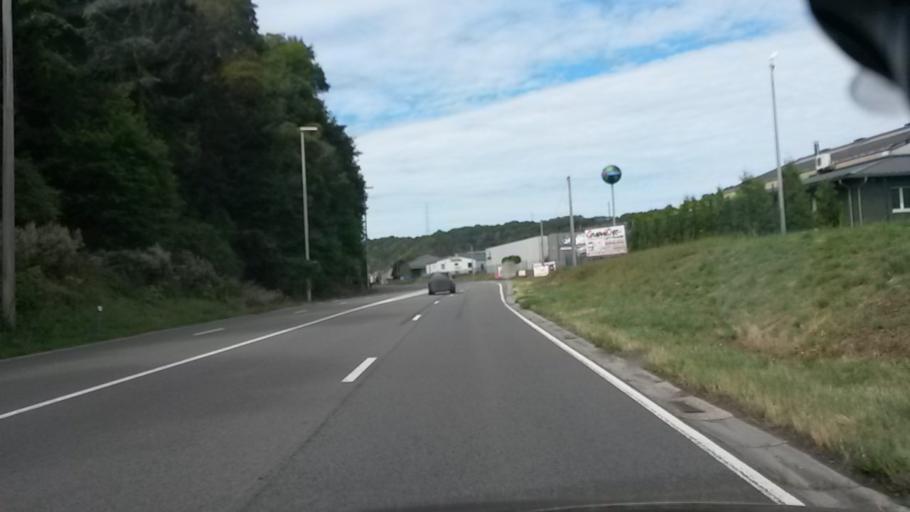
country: BE
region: Wallonia
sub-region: Province de Namur
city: Andenne
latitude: 50.4944
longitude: 5.0510
